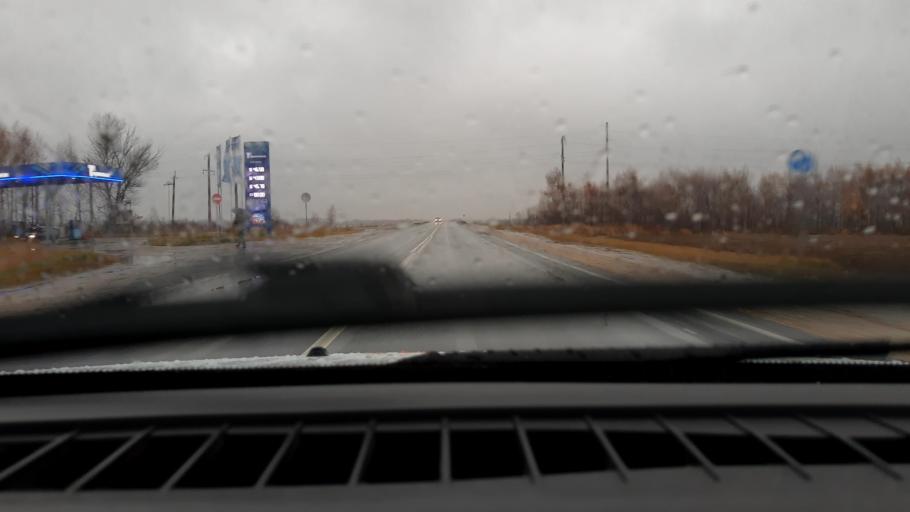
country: RU
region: Nizjnij Novgorod
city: Sitniki
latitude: 56.4914
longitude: 44.0226
